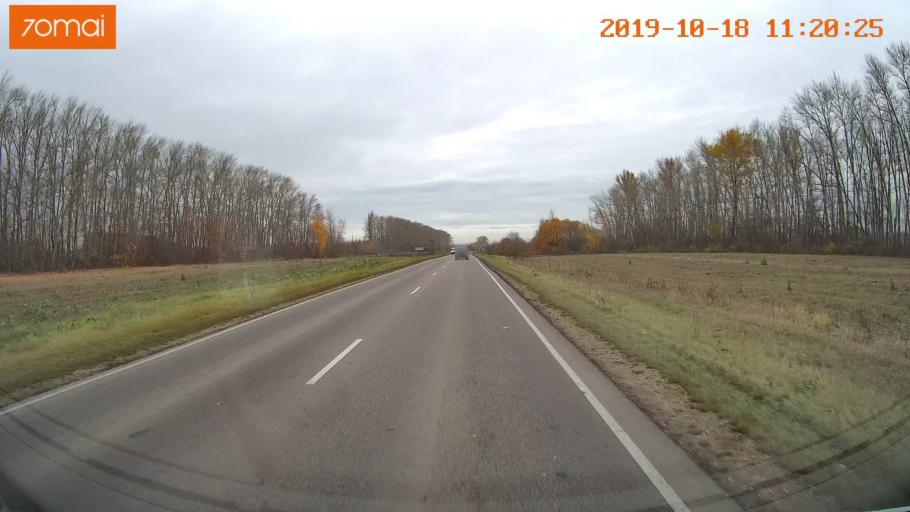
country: RU
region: Tula
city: Kimovsk
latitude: 54.0604
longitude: 38.5585
